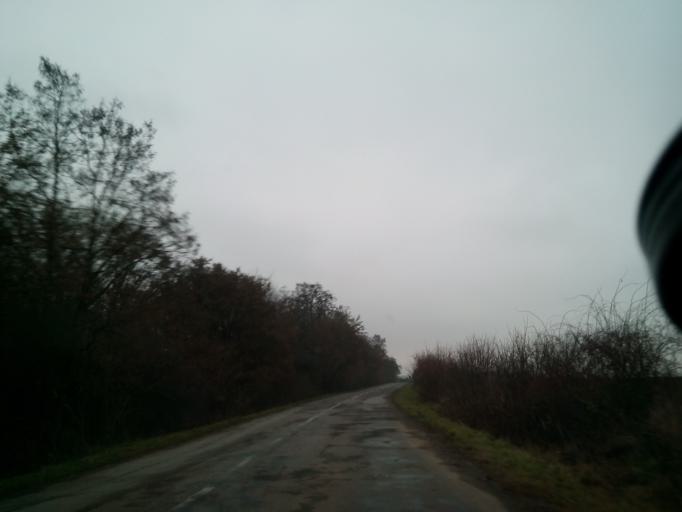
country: SK
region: Kosicky
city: Kosice
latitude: 48.7194
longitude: 21.4383
